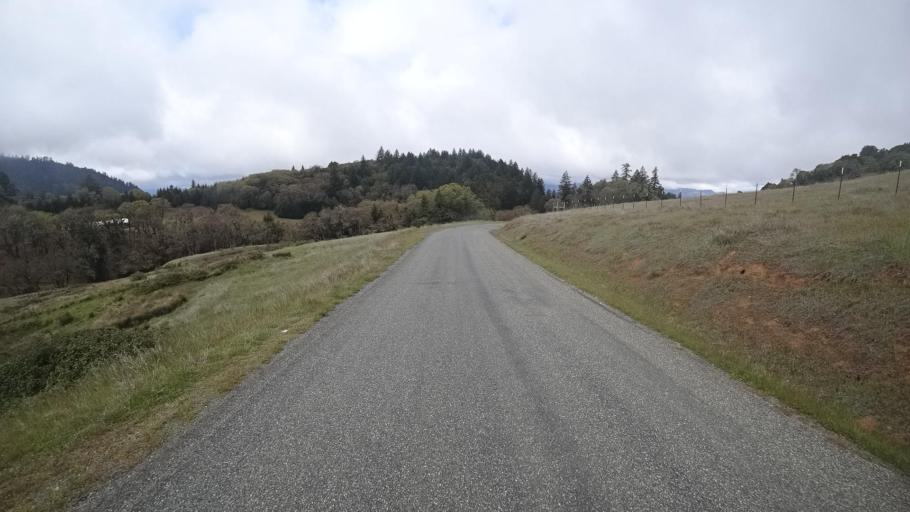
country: US
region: California
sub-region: Humboldt County
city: Redway
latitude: 40.1560
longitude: -123.5433
